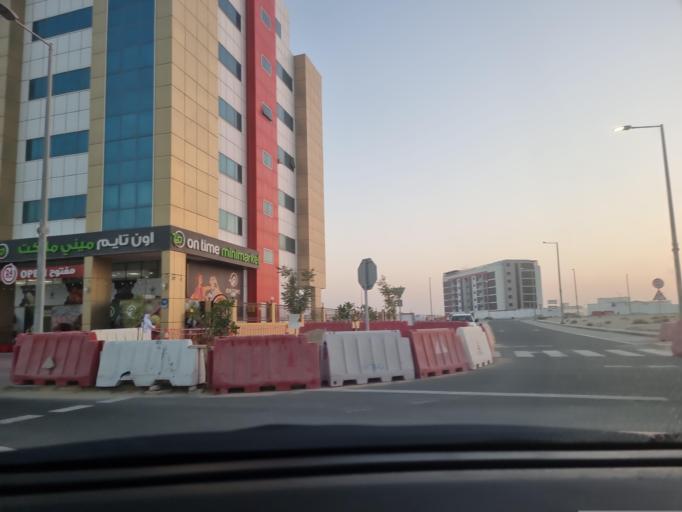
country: AE
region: Abu Dhabi
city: Abu Dhabi
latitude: 24.3687
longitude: 54.7400
